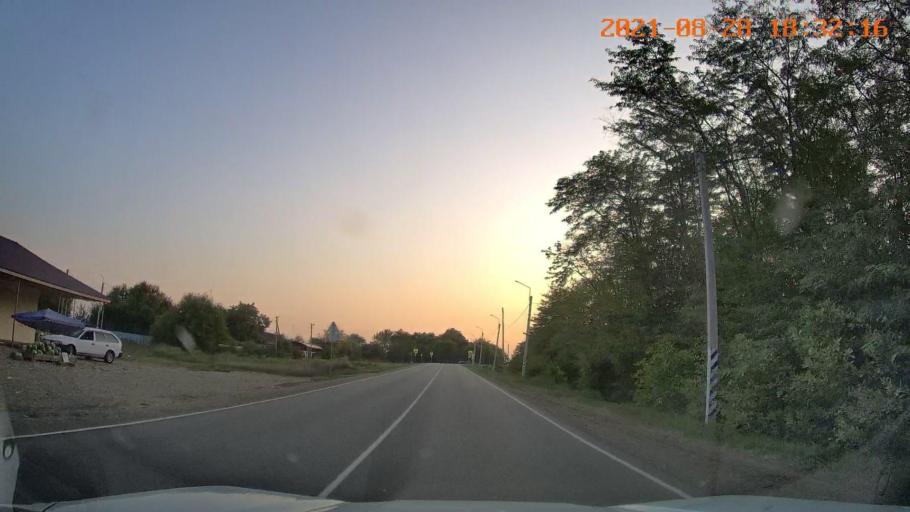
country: RU
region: Adygeya
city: Giaginskaya
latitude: 44.8772
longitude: 40.1923
